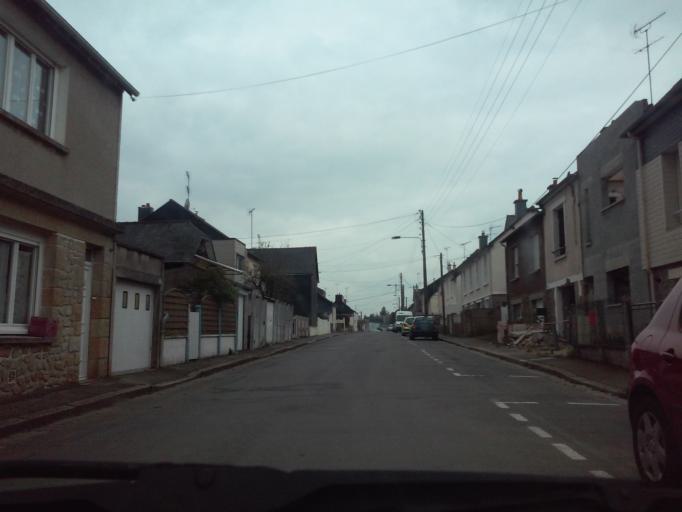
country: FR
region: Brittany
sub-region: Departement d'Ille-et-Vilaine
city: Fougeres
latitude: 48.3447
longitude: -1.1838
